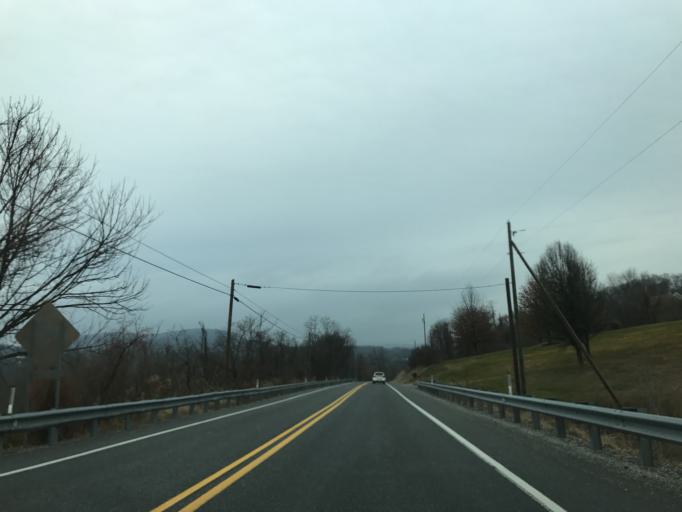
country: US
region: Maryland
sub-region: Frederick County
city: Emmitsburg
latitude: 39.7236
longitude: -77.3574
